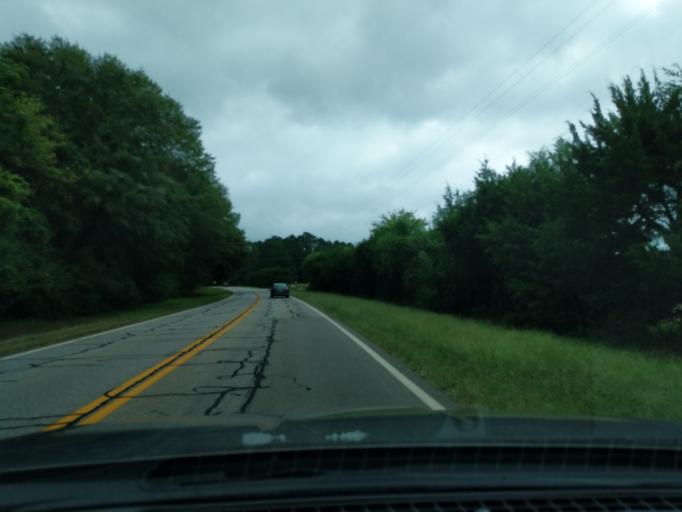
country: US
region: Georgia
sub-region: Columbia County
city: Appling
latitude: 33.6047
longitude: -82.3894
